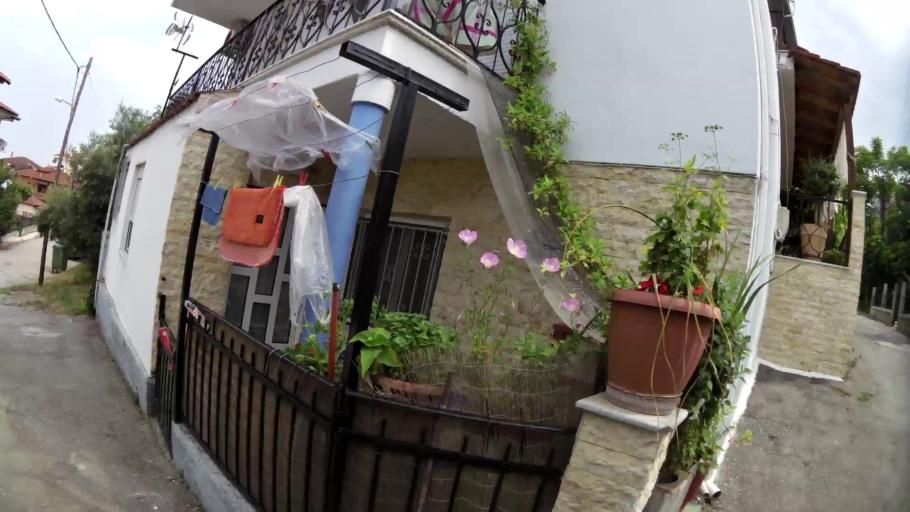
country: GR
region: Central Macedonia
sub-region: Nomos Imathias
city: Veroia
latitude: 40.5132
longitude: 22.2121
